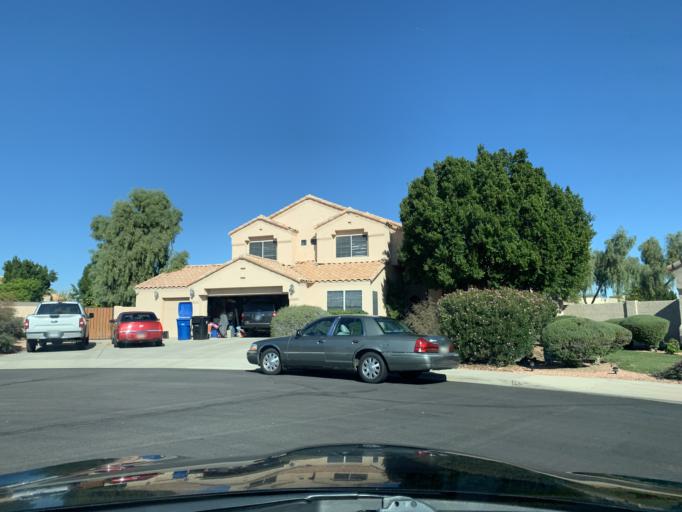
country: US
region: Arizona
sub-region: Pinal County
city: Apache Junction
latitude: 33.3843
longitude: -111.6181
